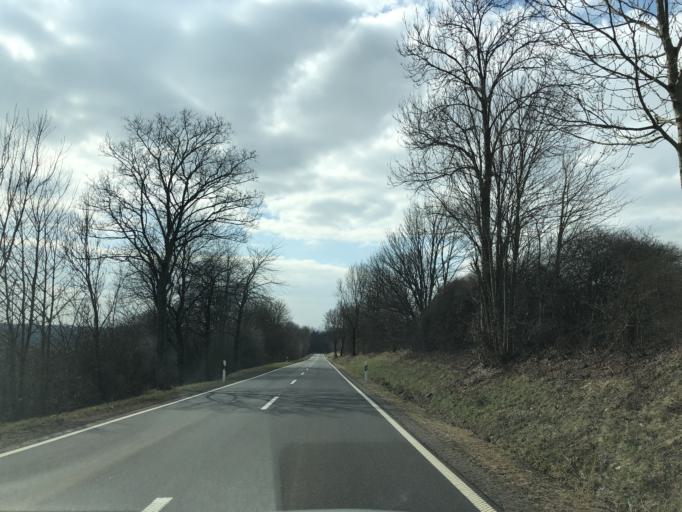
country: DE
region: Hesse
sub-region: Regierungsbezirk Giessen
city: Schotten
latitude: 50.5130
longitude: 9.1358
